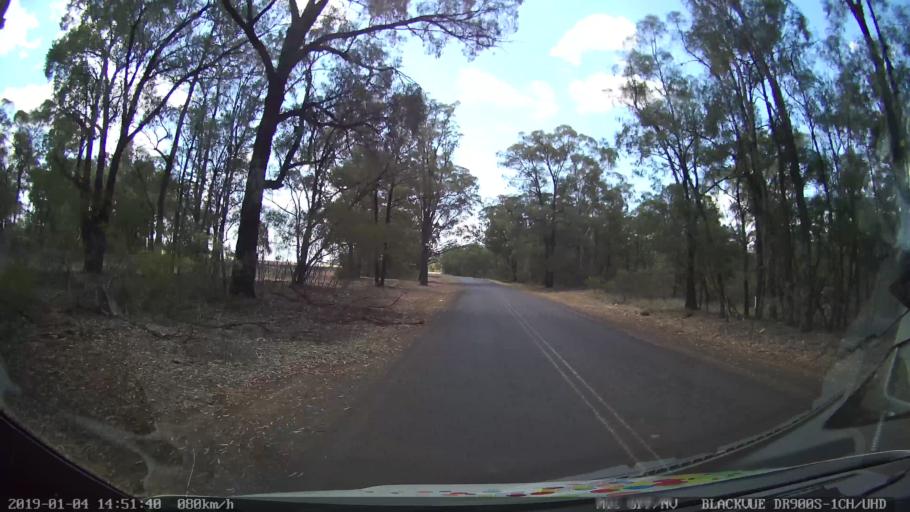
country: AU
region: New South Wales
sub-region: Dubbo Municipality
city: Dubbo
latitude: -32.0245
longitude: 148.6510
